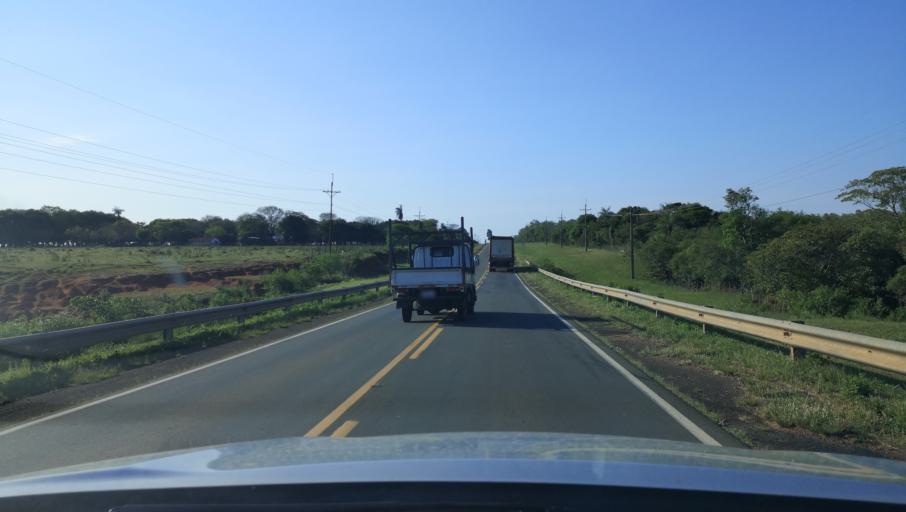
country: PY
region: Misiones
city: Santa Maria
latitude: -26.7704
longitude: -57.0308
